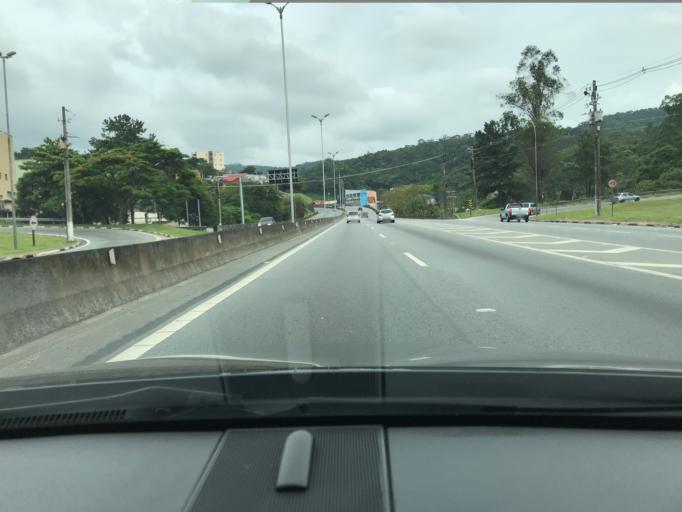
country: BR
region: Sao Paulo
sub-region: Cotia
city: Cotia
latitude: -23.6028
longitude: -46.9239
